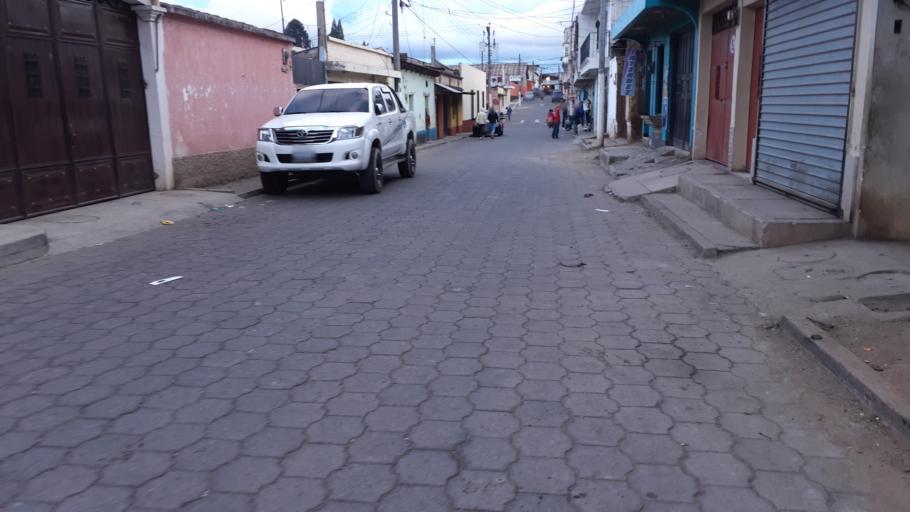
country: GT
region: Chimaltenango
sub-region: Municipio de Chimaltenango
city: Chimaltenango
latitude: 14.6635
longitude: -90.8202
